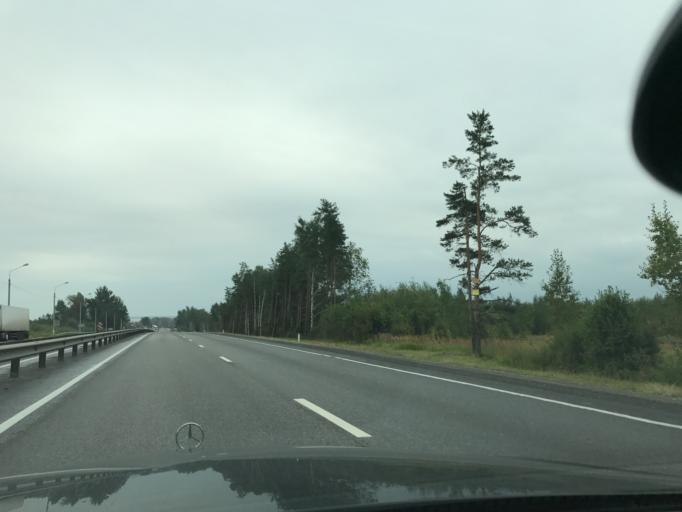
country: RU
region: Vladimir
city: Novovyazniki
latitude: 56.1867
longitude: 42.3959
